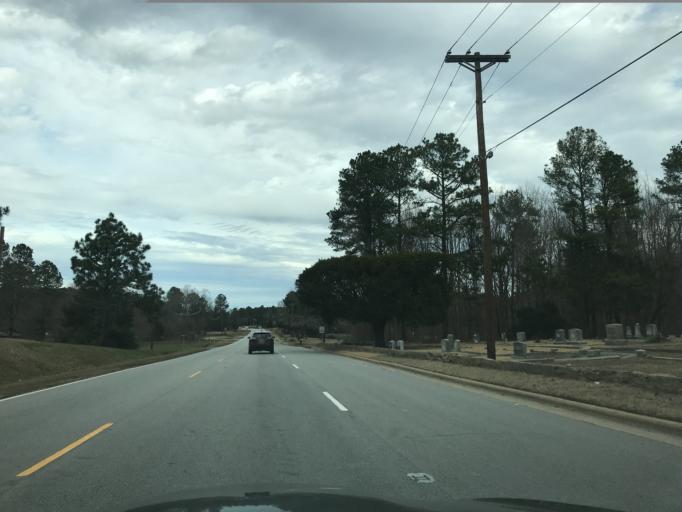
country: US
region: North Carolina
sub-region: Franklin County
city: Louisburg
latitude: 36.1227
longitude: -78.2947
